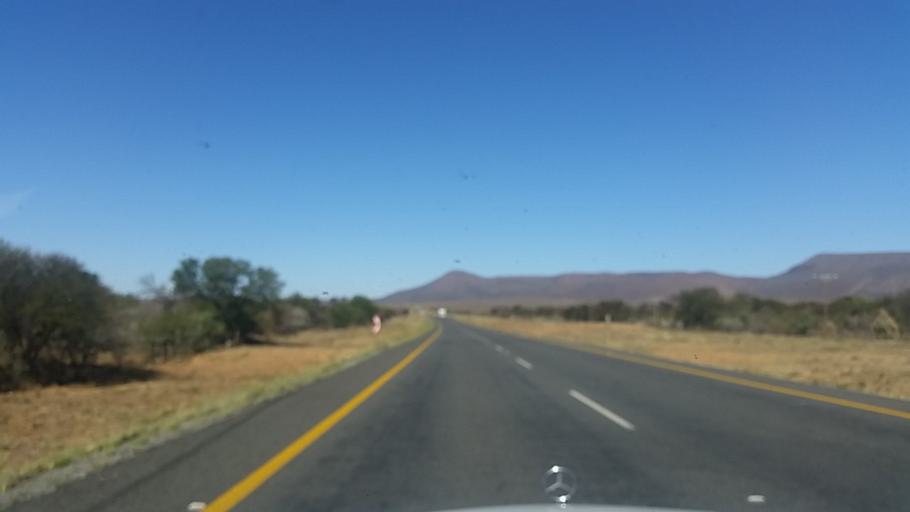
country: ZA
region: Eastern Cape
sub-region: Cacadu District Municipality
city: Graaff-Reinet
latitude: -32.0029
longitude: 24.6636
